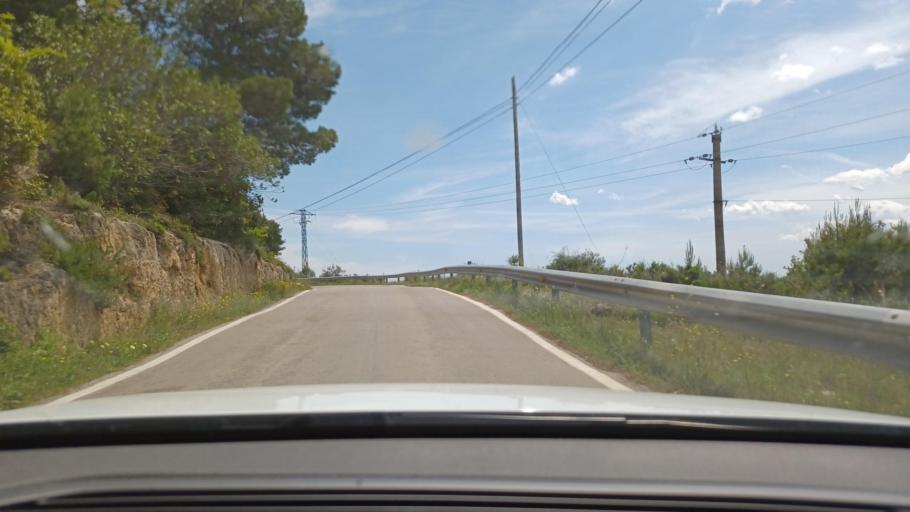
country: ES
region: Valencia
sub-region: Provincia de Castello
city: Rosell
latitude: 40.6457
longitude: 0.2698
